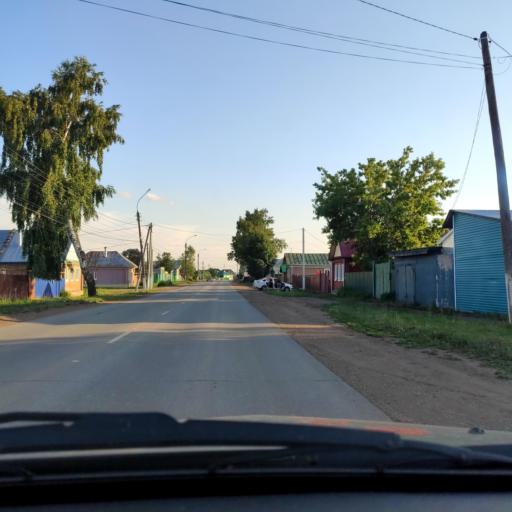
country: RU
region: Bashkortostan
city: Blagoveshchensk
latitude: 55.0345
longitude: 55.9915
